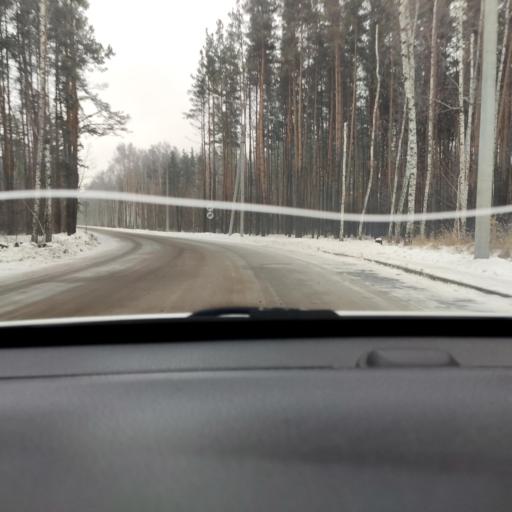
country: RU
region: Voronezj
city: Somovo
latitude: 51.6947
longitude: 39.2806
